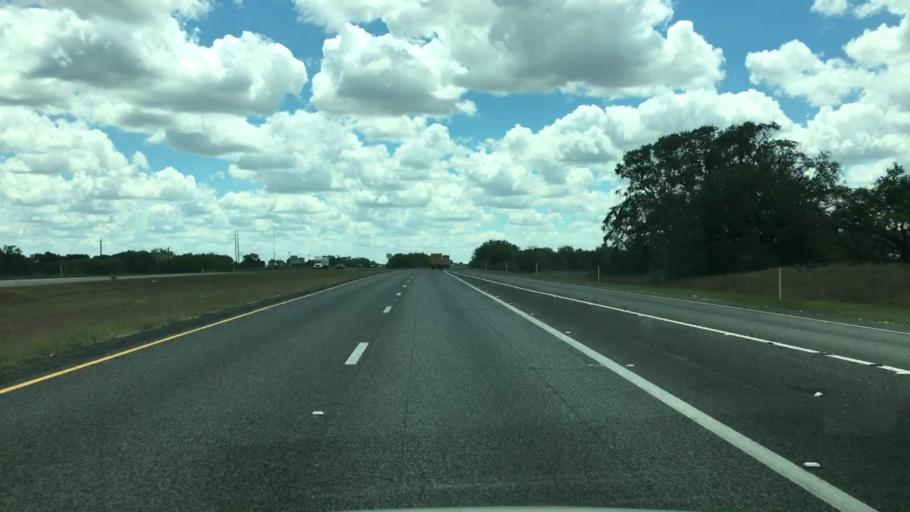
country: US
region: Texas
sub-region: Atascosa County
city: Pleasanton
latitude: 28.9435
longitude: -98.4367
